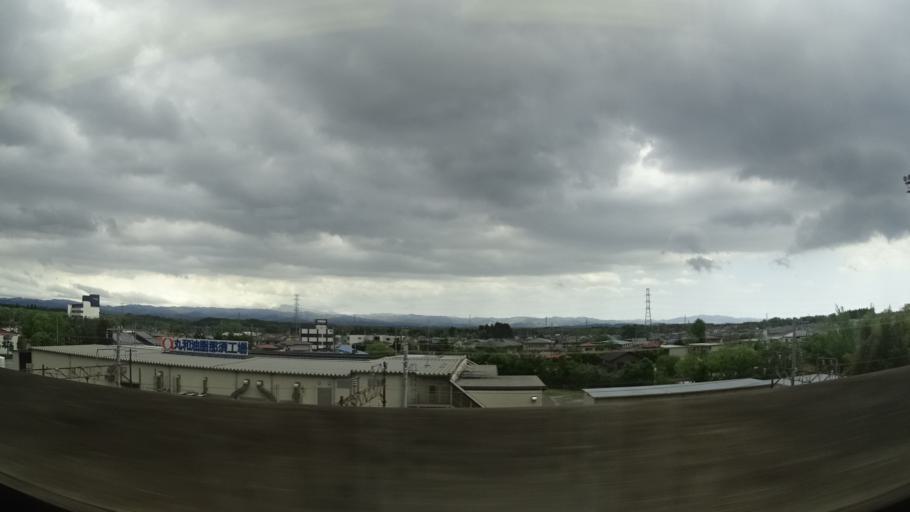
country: JP
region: Tochigi
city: Kuroiso
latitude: 36.9734
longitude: 140.0626
